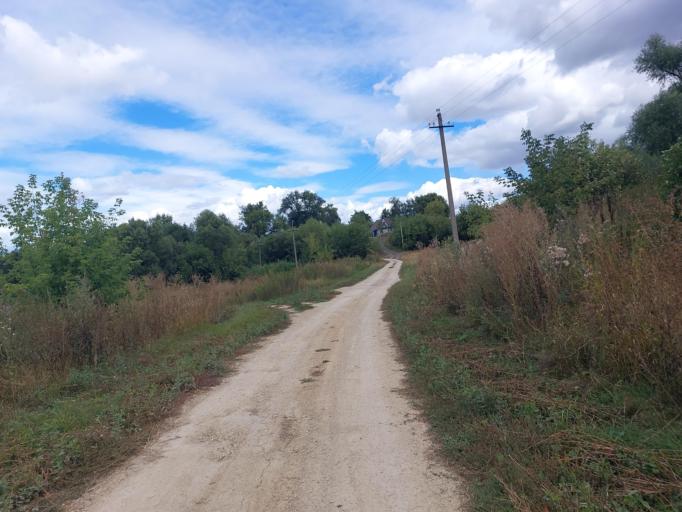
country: RU
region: Lipetsk
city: Terbuny
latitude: 52.2620
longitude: 38.2067
